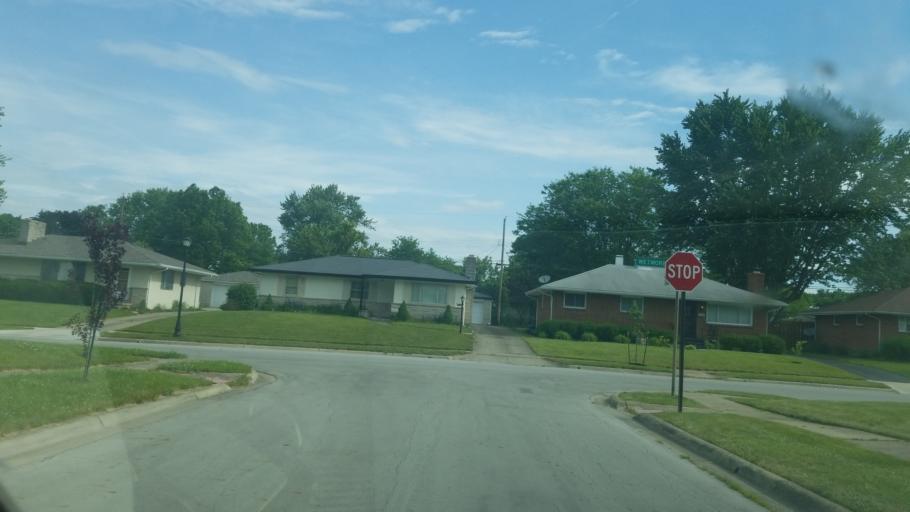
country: US
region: Ohio
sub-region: Franklin County
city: Worthington
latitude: 40.0572
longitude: -82.9908
